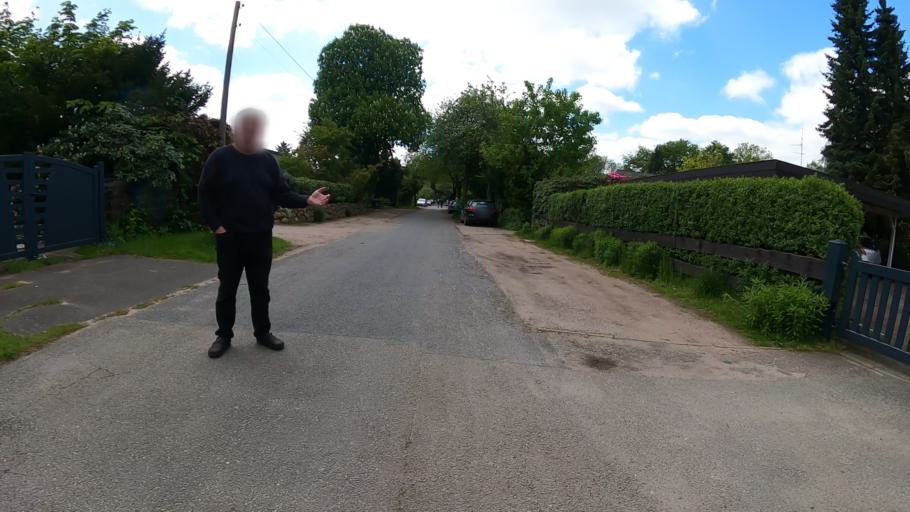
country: DE
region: Hamburg
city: Bergstedt
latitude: 53.6763
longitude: 10.1109
